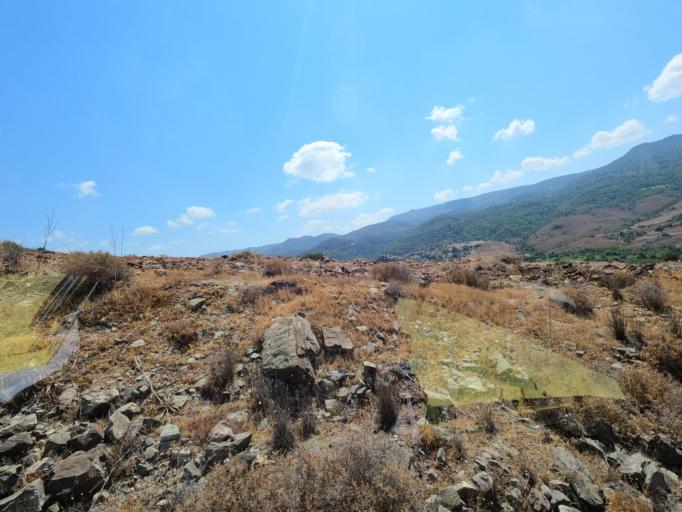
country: CY
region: Limassol
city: Pachna
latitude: 34.7916
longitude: 32.6852
